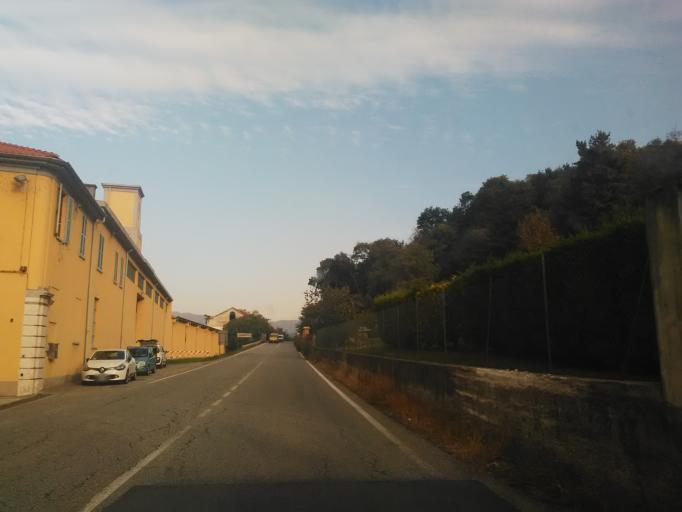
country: IT
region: Piedmont
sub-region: Provincia di Novara
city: Prato Sesia
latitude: 45.6402
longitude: 8.3768
